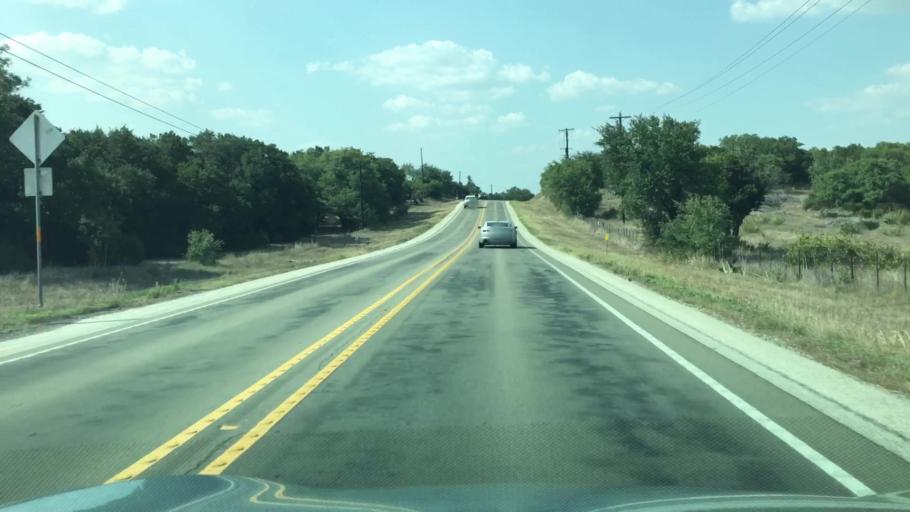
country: US
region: Texas
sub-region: Hays County
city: Woodcreek
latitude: 30.0843
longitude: -98.1002
